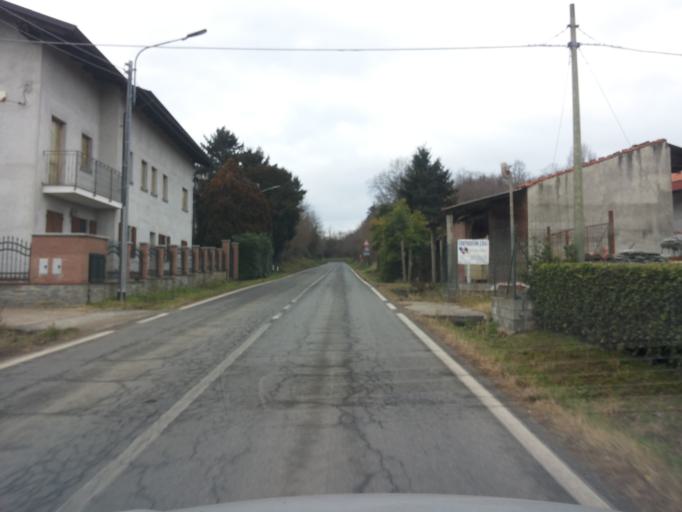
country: IT
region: Piedmont
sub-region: Provincia di Vercelli
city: Moncrivello
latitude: 45.3335
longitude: 8.0010
